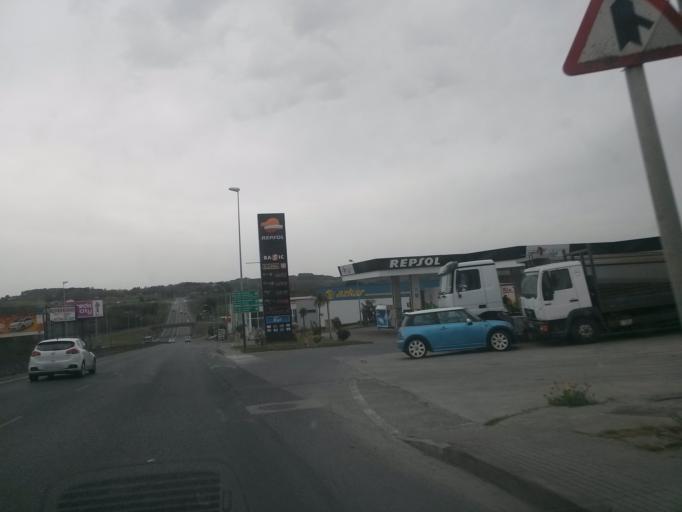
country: ES
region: Galicia
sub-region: Provincia de Lugo
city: Lugo
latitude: 43.0505
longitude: -7.5663
